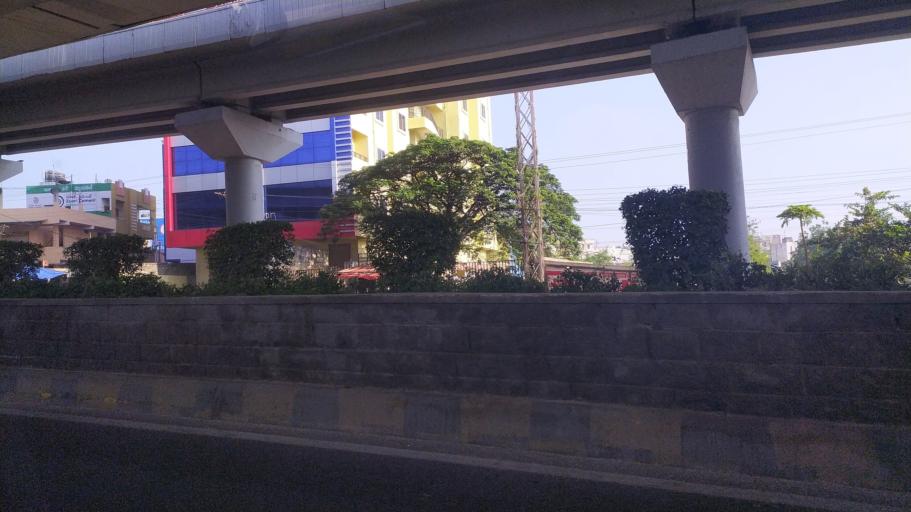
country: IN
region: Telangana
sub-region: Hyderabad
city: Hyderabad
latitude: 17.3250
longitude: 78.4275
